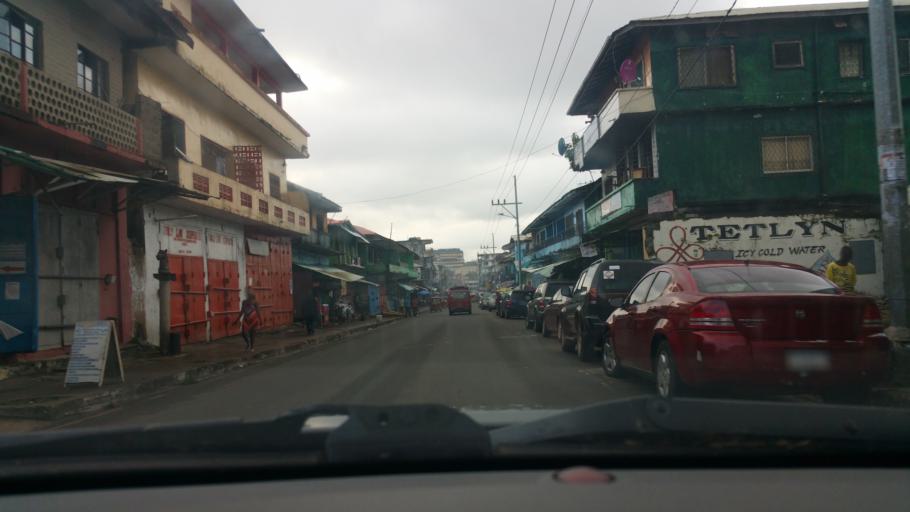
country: LR
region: Montserrado
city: Monrovia
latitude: 6.3098
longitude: -10.8004
